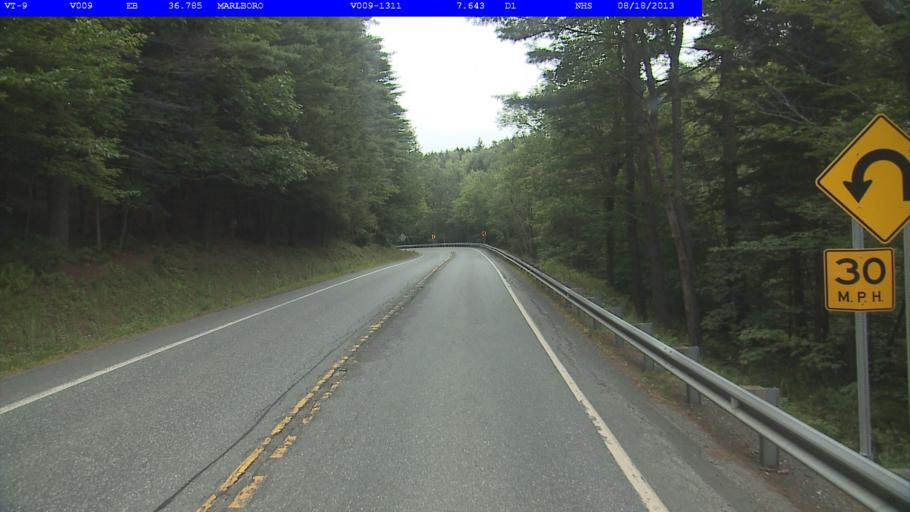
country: US
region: Vermont
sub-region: Windham County
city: West Brattleboro
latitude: 42.8768
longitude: -72.6886
